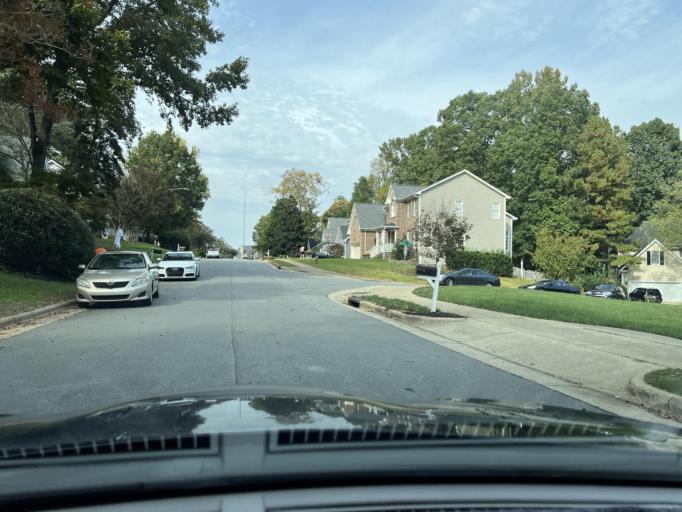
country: US
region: North Carolina
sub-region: Wake County
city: Wake Forest
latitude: 35.8963
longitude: -78.5834
